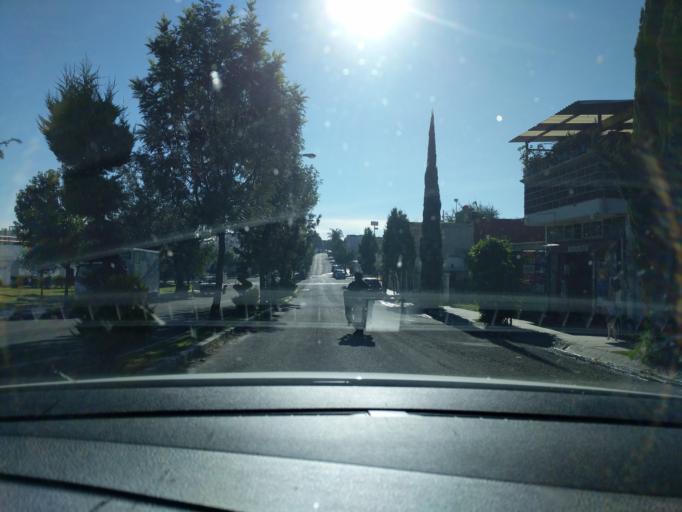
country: MX
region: Puebla
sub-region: Huejotzingo
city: Los Encinos
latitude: 19.1775
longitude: -98.3933
